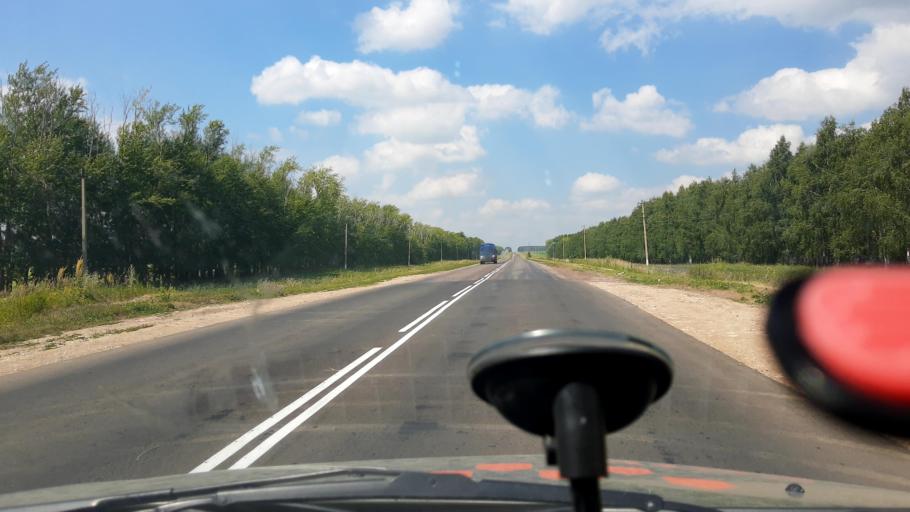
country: RU
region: Bashkortostan
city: Chekmagush
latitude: 54.9150
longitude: 54.5833
